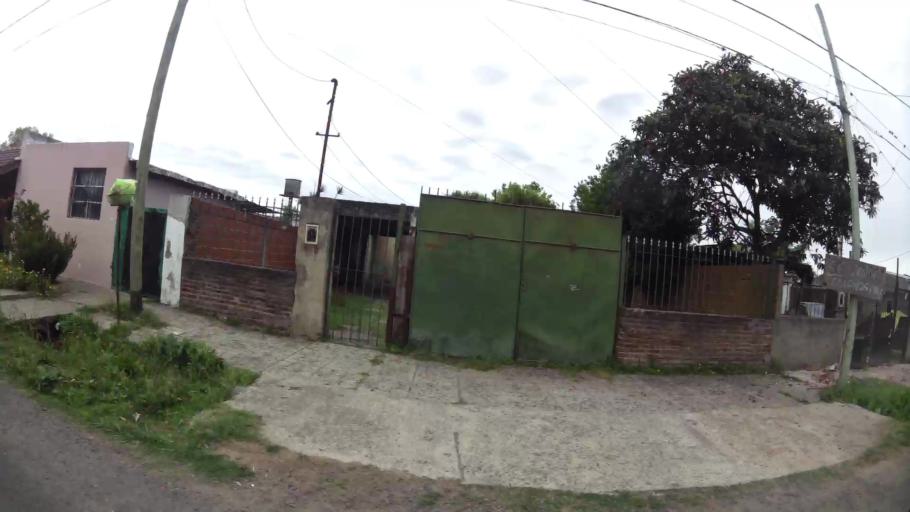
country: AR
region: Buenos Aires
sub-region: Partido de Campana
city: Campana
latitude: -34.1816
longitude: -58.9356
